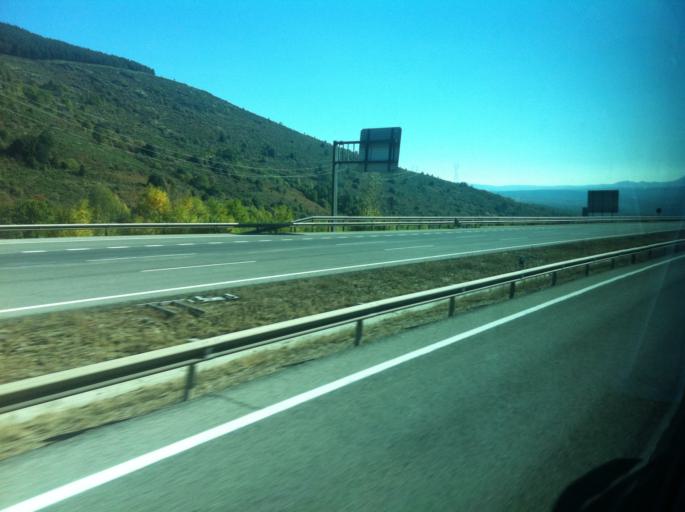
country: ES
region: Madrid
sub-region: Provincia de Madrid
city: Robregordo
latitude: 41.1186
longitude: -3.5864
